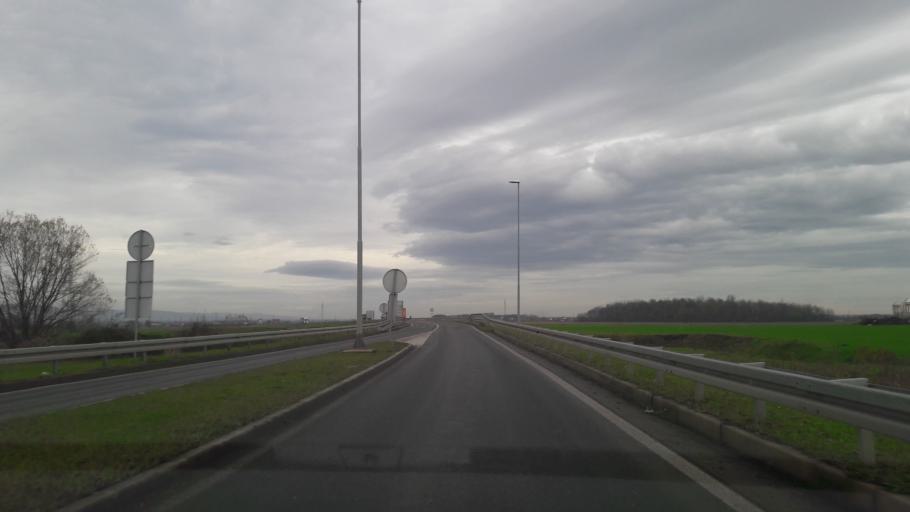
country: HR
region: Osjecko-Baranjska
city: Velimirovac
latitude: 45.5094
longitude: 18.1156
